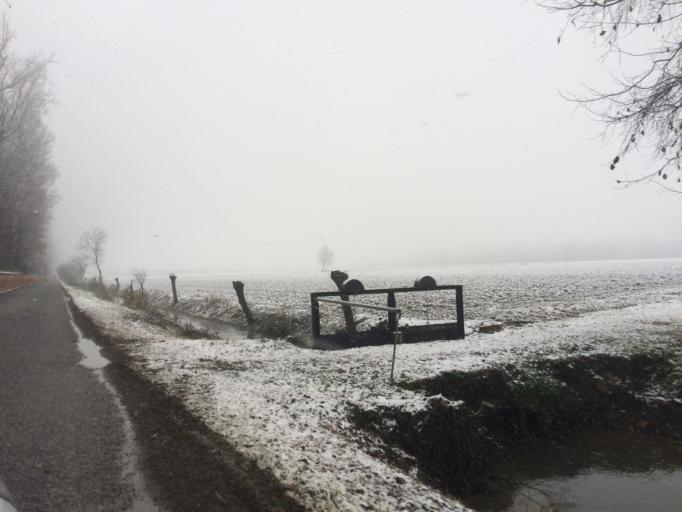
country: IT
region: Piedmont
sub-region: Provincia di Cuneo
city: Racconigi
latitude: 44.7857
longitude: 7.6667
